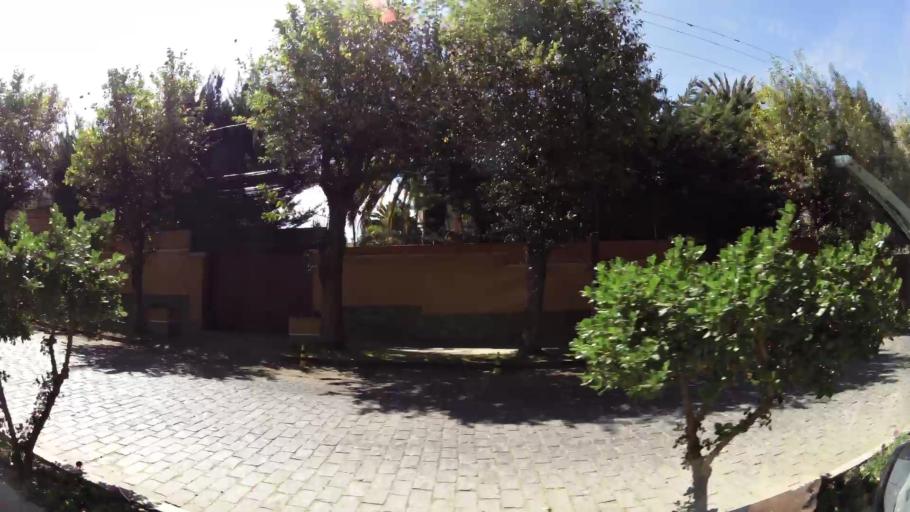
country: BO
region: La Paz
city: La Paz
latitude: -16.5437
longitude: -68.0919
